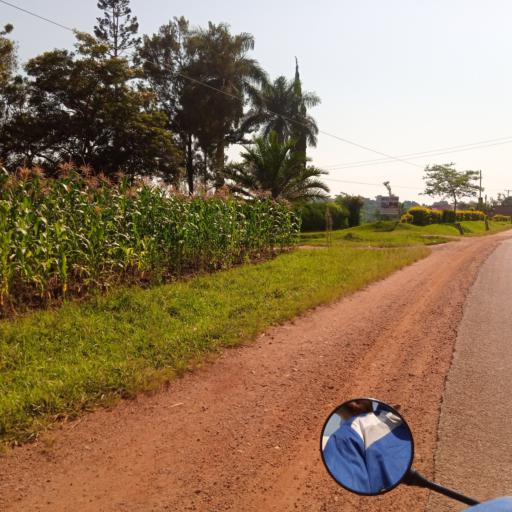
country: UG
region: Central Region
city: Masaka
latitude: -0.3788
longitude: 31.7063
